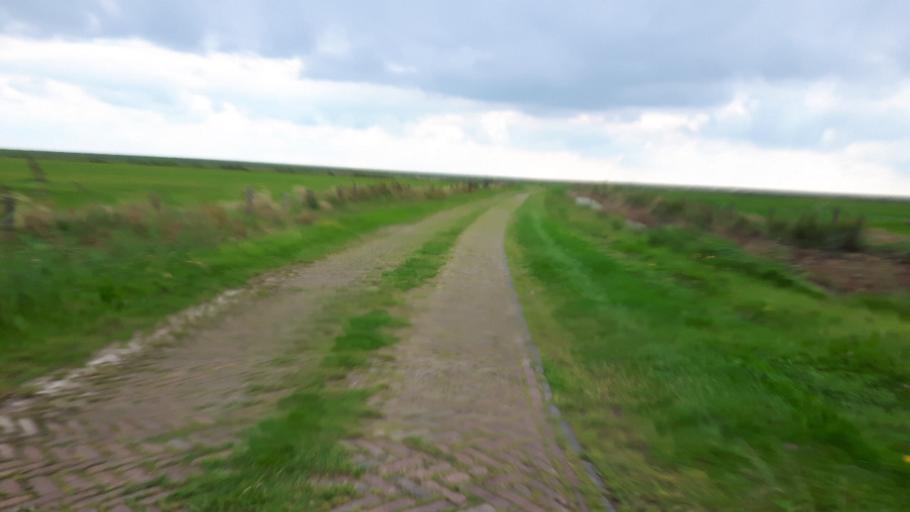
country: NL
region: Friesland
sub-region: Gemeente Ameland
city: Nes
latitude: 53.4481
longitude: 5.8194
